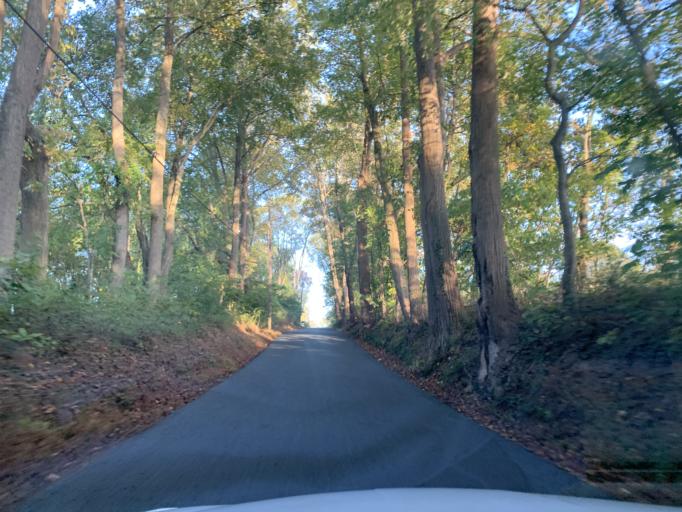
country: US
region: Maryland
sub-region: Harford County
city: Fallston
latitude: 39.5112
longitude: -76.4161
